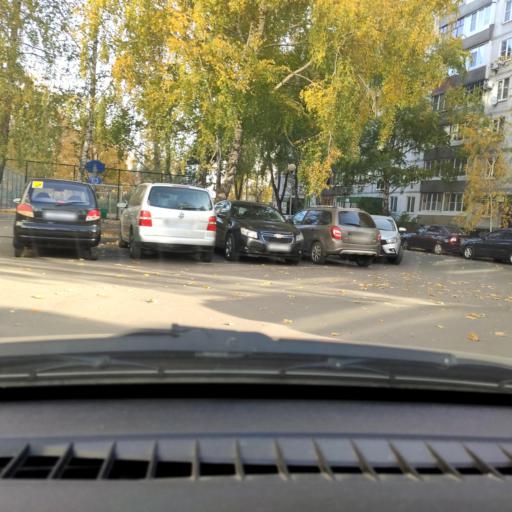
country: RU
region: Samara
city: Tol'yatti
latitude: 53.5118
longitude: 49.2608
